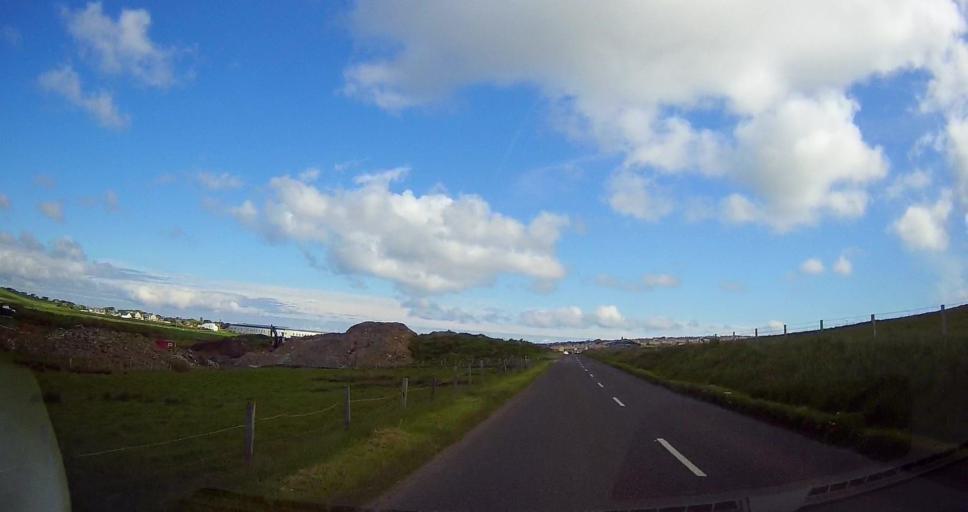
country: GB
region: Scotland
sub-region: Orkney Islands
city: Orkney
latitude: 58.9674
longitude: -2.9642
